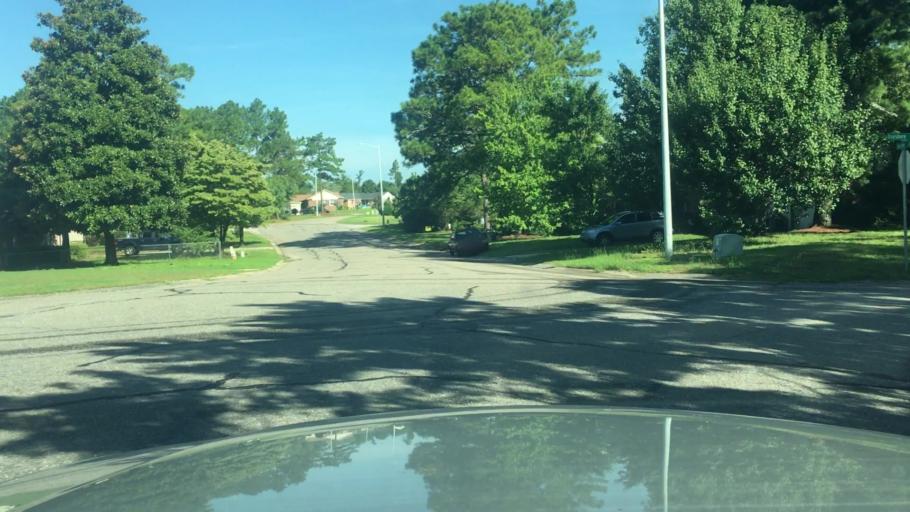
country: US
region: North Carolina
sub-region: Cumberland County
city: Spring Lake
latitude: 35.1419
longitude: -78.9011
